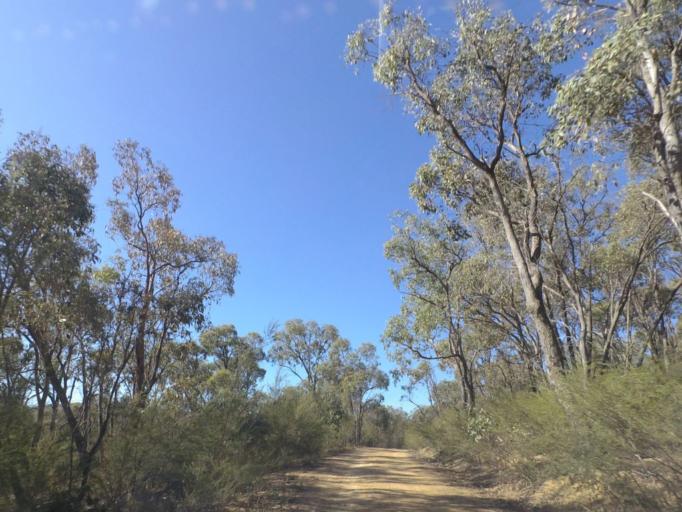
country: AU
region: Victoria
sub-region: Murrindindi
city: Kinglake West
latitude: -37.4674
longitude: 145.3649
